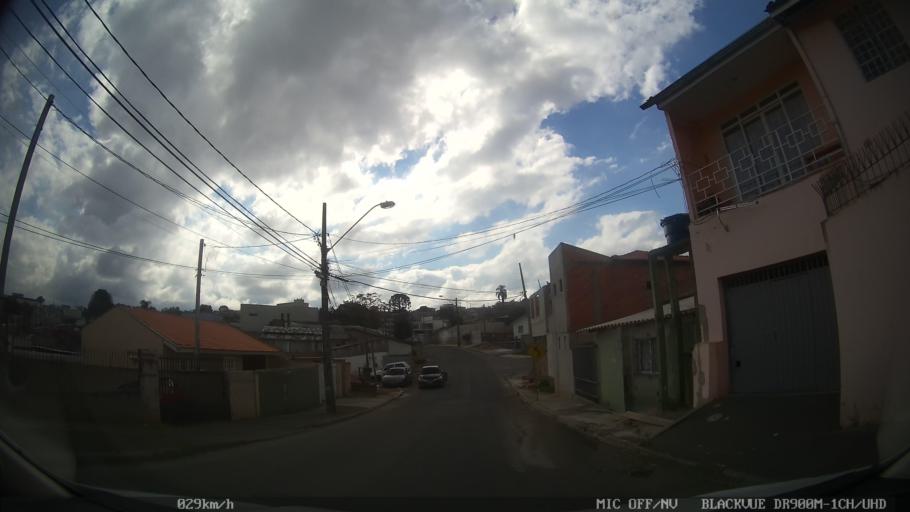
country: BR
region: Parana
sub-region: Colombo
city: Colombo
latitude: -25.3544
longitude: -49.1936
